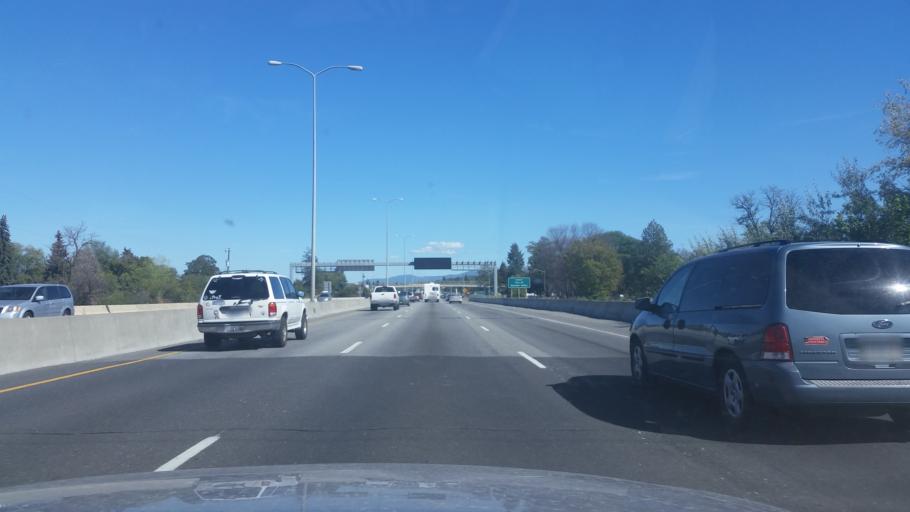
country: US
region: Washington
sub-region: Spokane County
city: Millwood
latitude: 47.6538
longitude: -117.3471
